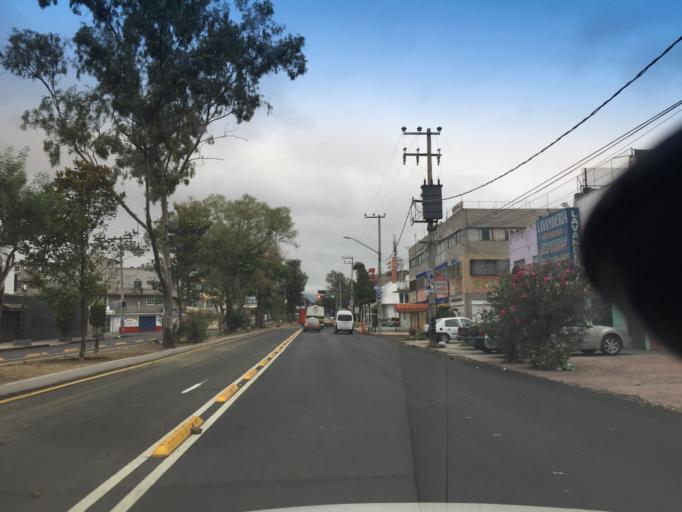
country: MX
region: Mexico City
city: Venustiano Carranza
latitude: 19.4714
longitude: -99.0669
